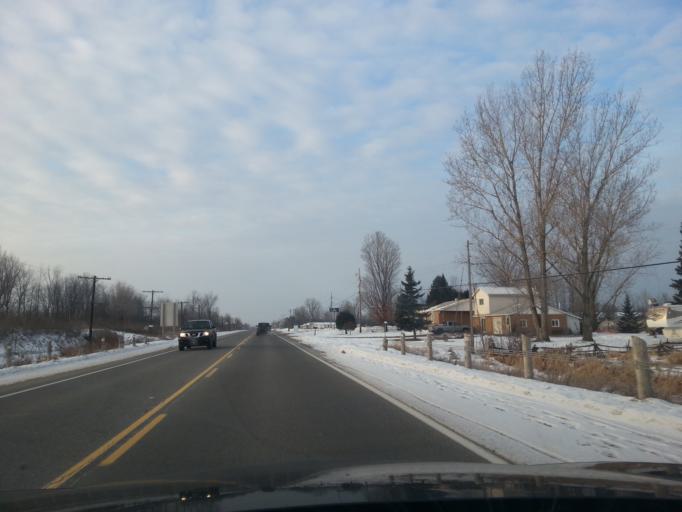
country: CA
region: Ontario
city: Perth
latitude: 44.9031
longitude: -76.2796
